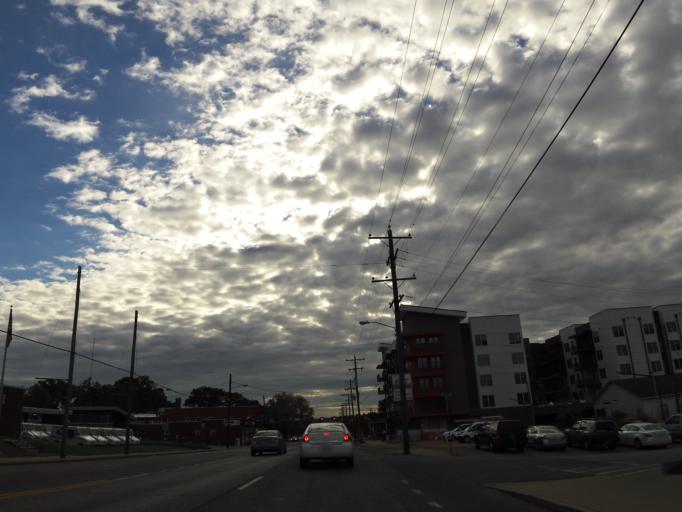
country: US
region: Tennessee
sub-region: Davidson County
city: Nashville
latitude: 36.1524
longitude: -86.8405
